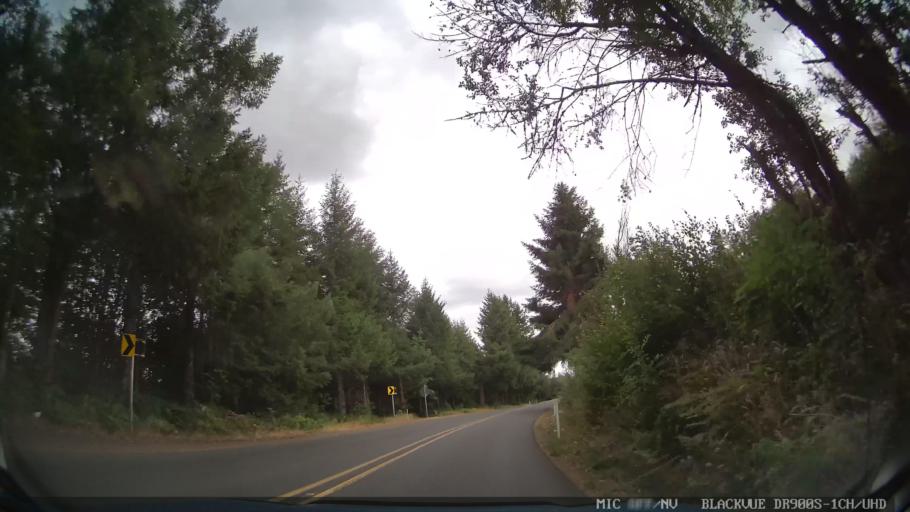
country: US
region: Oregon
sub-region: Linn County
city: Lyons
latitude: 44.8532
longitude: -122.6796
